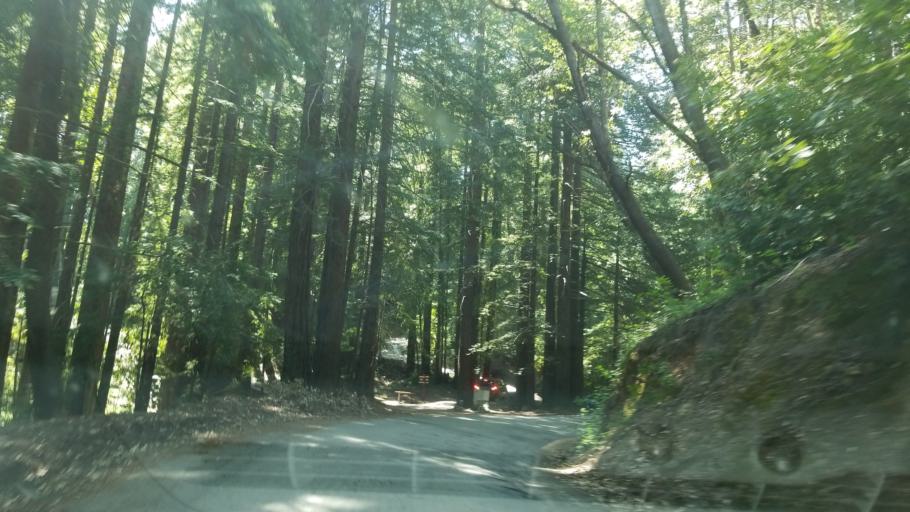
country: US
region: California
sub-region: Santa Cruz County
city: Day Valley
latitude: 37.0583
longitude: -121.8210
